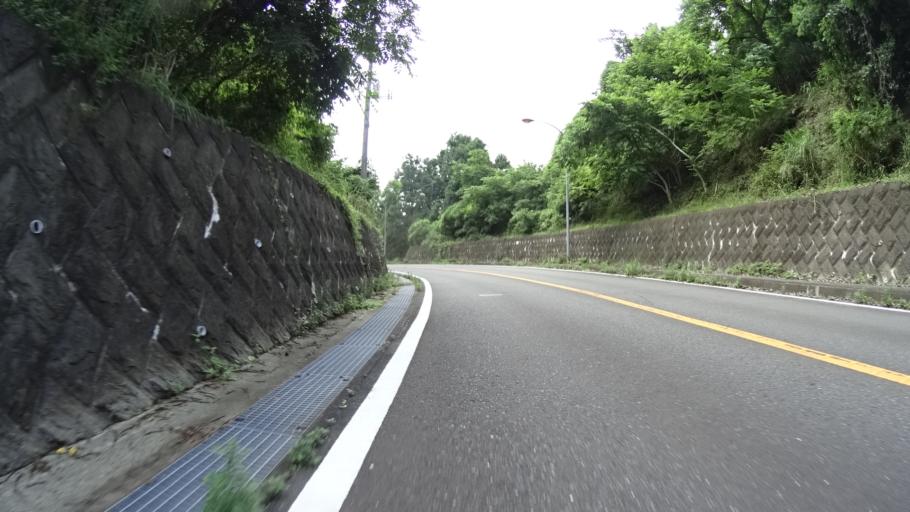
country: JP
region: Kanagawa
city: Hadano
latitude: 35.5165
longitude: 139.2324
